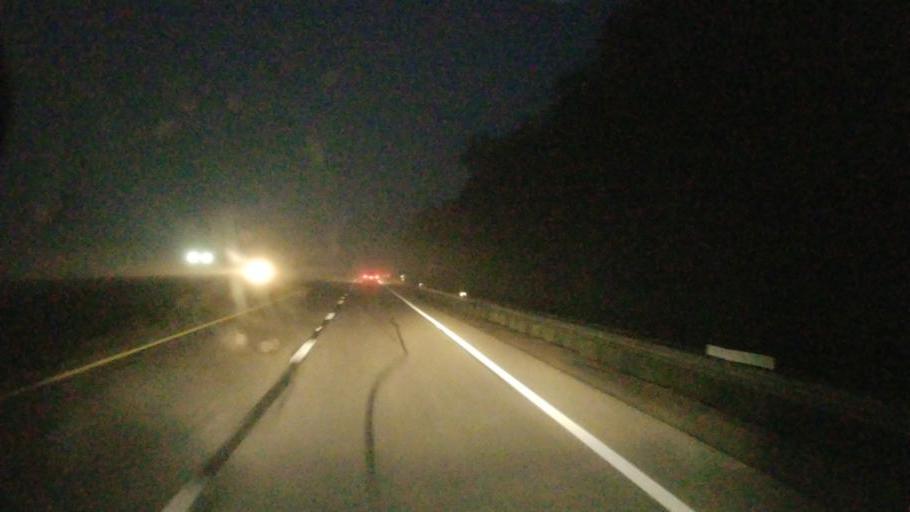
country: US
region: Ohio
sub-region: Ross County
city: Kingston
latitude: 39.4944
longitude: -82.9737
